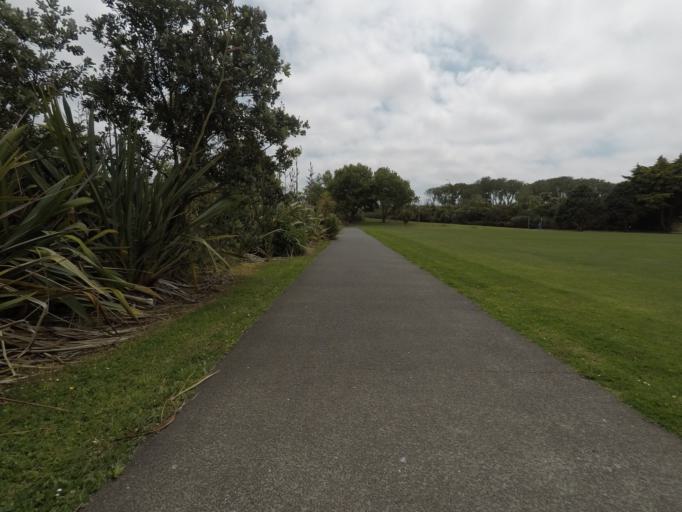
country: NZ
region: Auckland
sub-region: Auckland
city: Auckland
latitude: -36.9142
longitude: 174.7426
